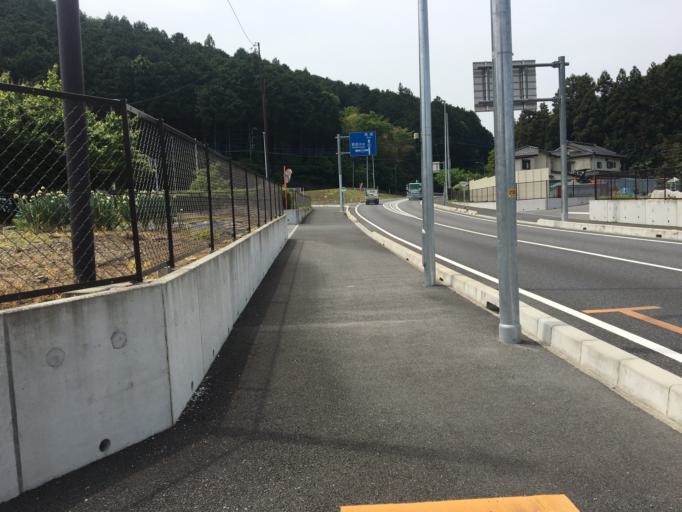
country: JP
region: Saitama
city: Hanno
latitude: 35.8552
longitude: 139.3019
